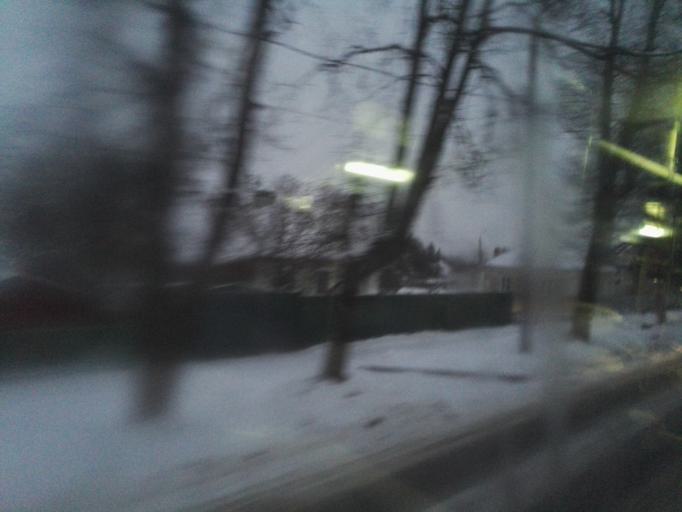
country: RU
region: Tula
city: Tula
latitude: 54.1680
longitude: 37.6028
